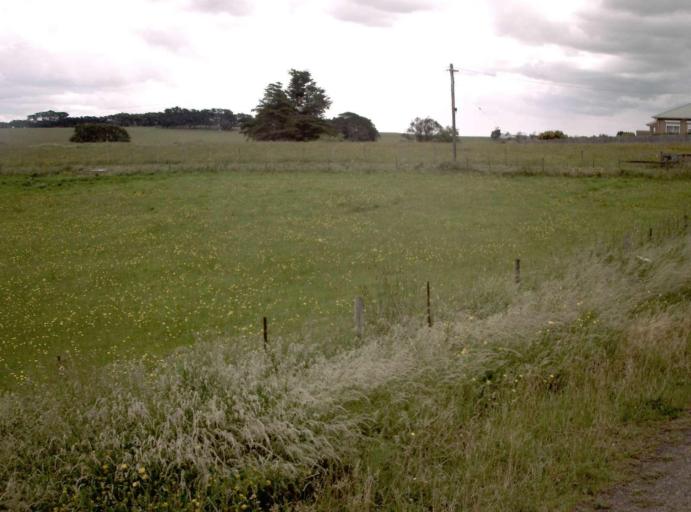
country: AU
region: Victoria
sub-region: Baw Baw
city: Warragul
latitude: -38.1364
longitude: 145.9348
